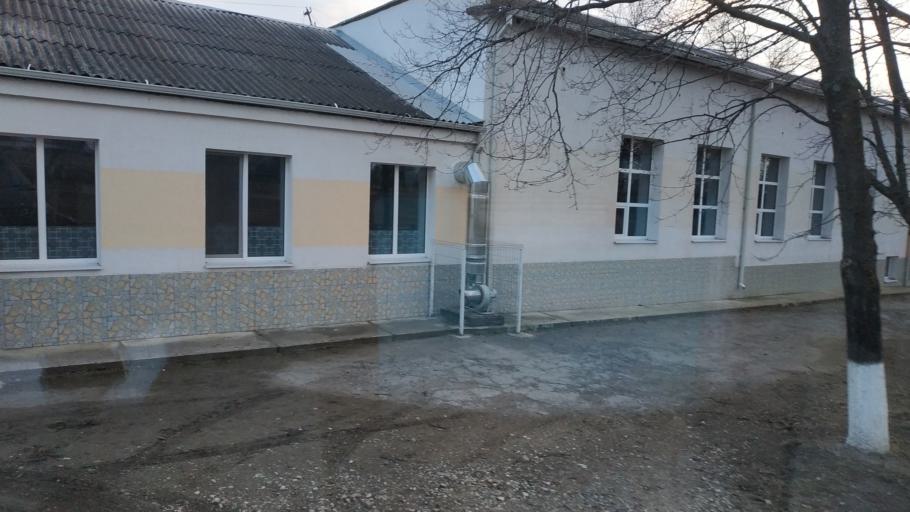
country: MD
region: Hincesti
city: Dancu
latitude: 46.6723
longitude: 28.3231
